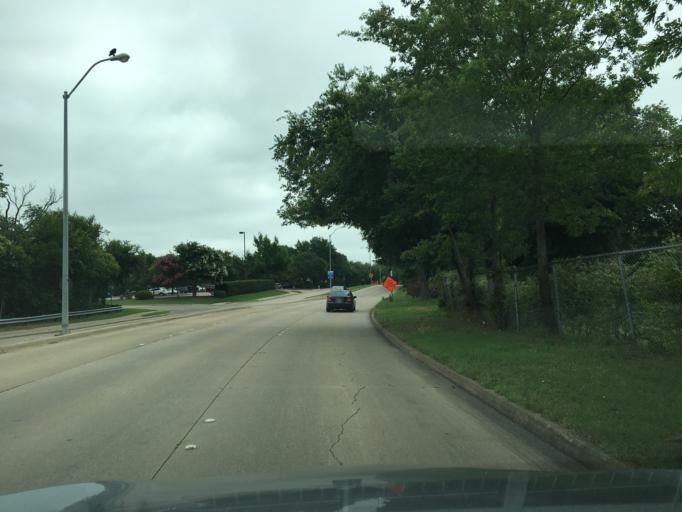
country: US
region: Texas
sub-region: Dallas County
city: Richardson
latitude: 32.9361
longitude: -96.7385
